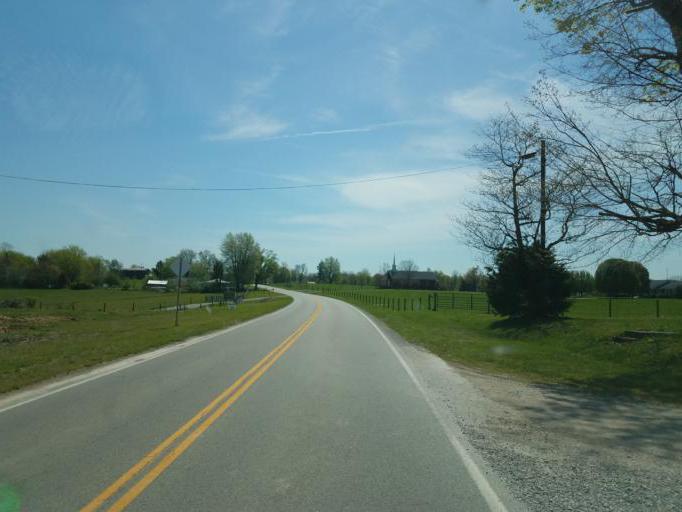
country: US
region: Kentucky
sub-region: Barren County
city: Cave City
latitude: 37.1503
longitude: -86.0442
